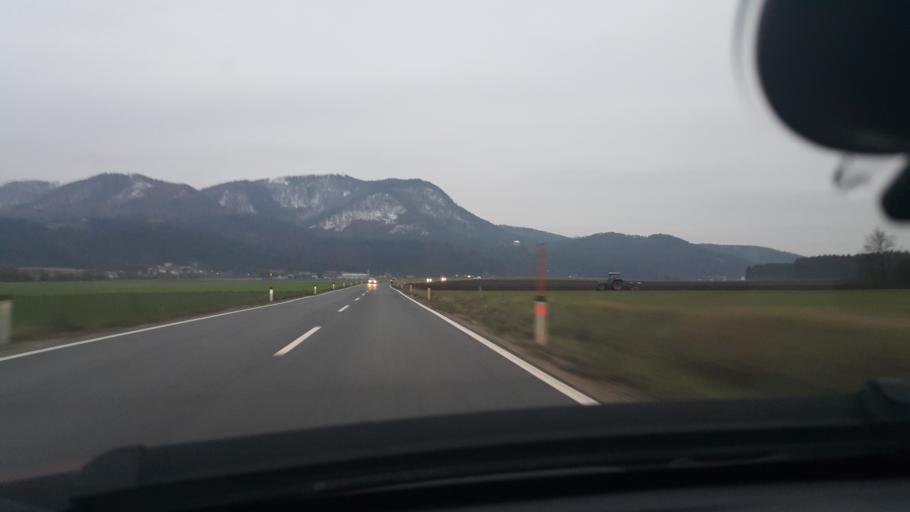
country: AT
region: Carinthia
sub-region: Politischer Bezirk Volkermarkt
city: Ruden
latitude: 46.6807
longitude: 14.7573
